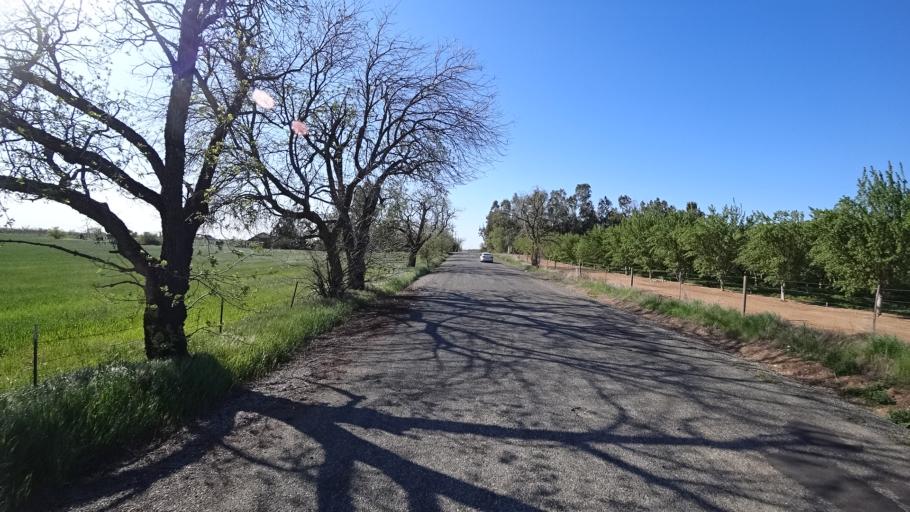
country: US
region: California
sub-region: Glenn County
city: Hamilton City
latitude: 39.7845
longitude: -122.0665
